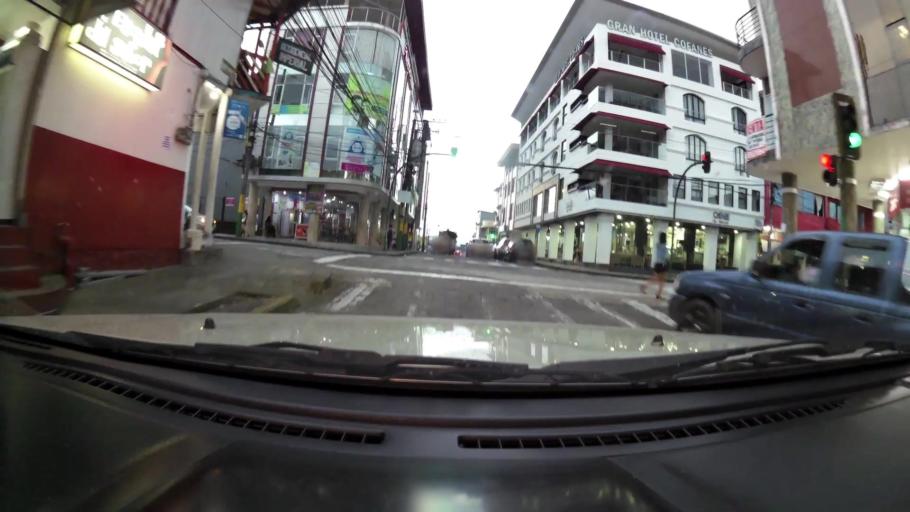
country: EC
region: Pastaza
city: Puyo
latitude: -1.4858
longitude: -77.9986
